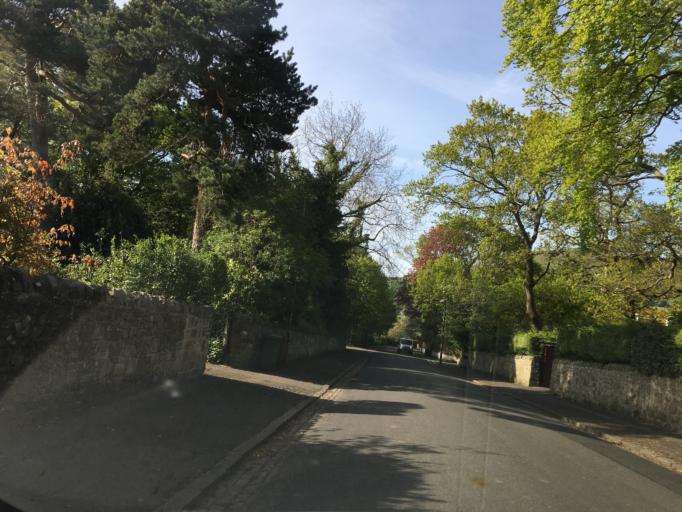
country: GB
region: Scotland
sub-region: Midlothian
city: Loanhead
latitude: 55.8991
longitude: -3.1982
